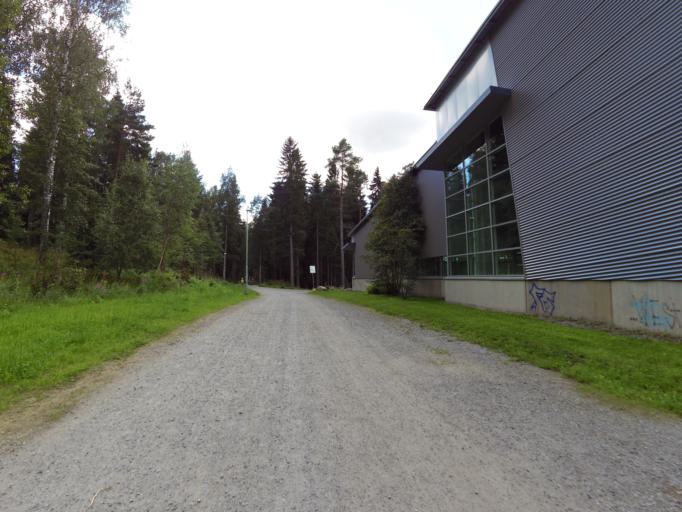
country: FI
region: Pirkanmaa
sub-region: Tampere
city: Yloejaervi
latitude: 61.5102
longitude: 23.6165
